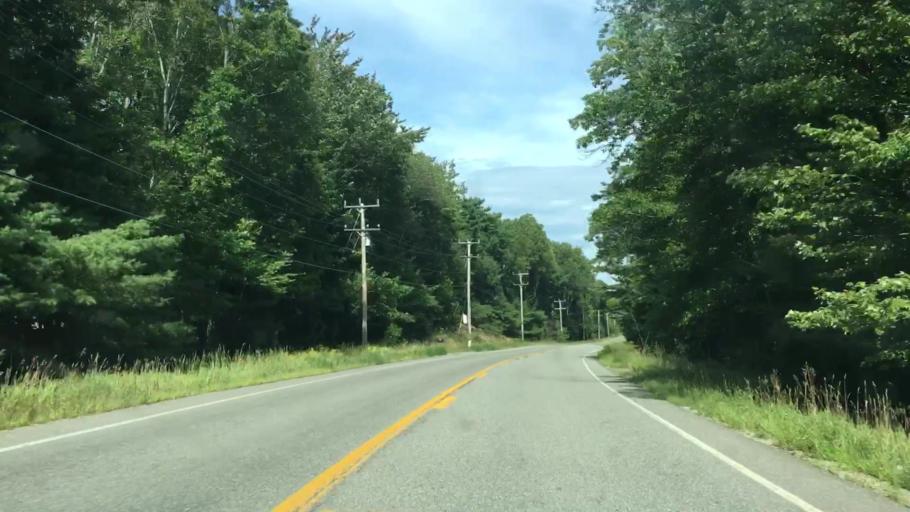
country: US
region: Maine
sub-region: Penobscot County
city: Lincoln
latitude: 45.4009
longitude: -68.5084
